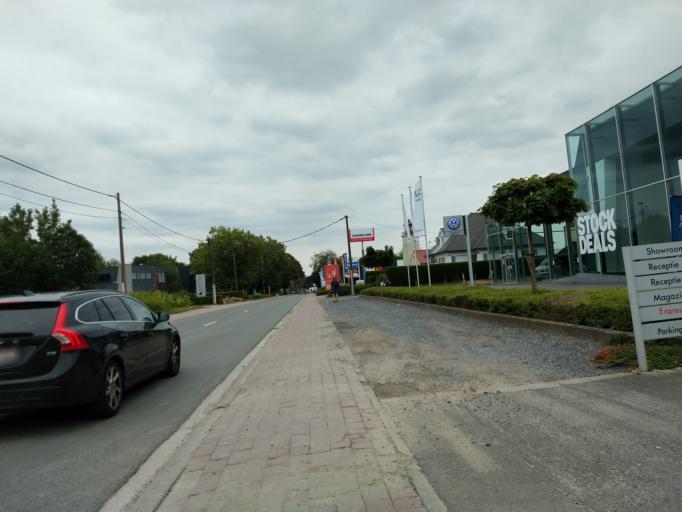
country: BE
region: Flanders
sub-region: Provincie Vlaams-Brabant
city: Overijse
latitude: 50.7809
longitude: 4.5140
